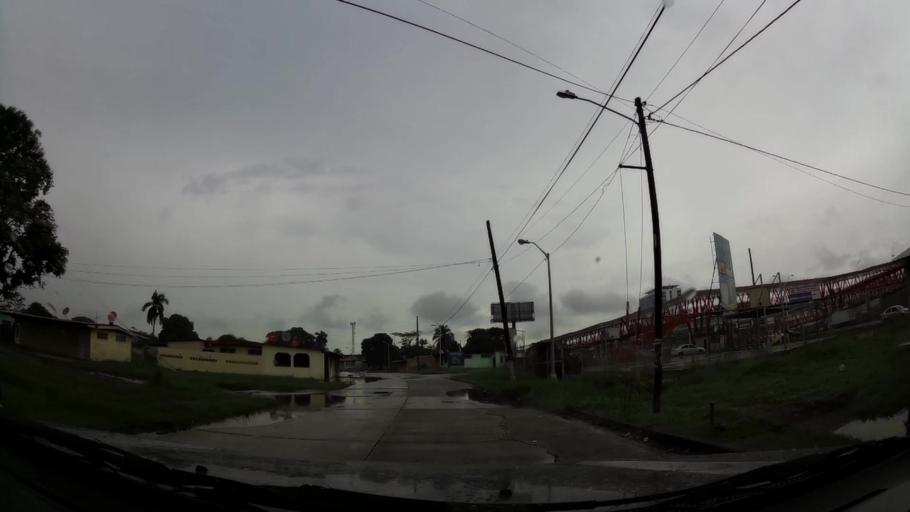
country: PA
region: Colon
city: Arco Iris
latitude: 9.3428
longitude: -79.8918
